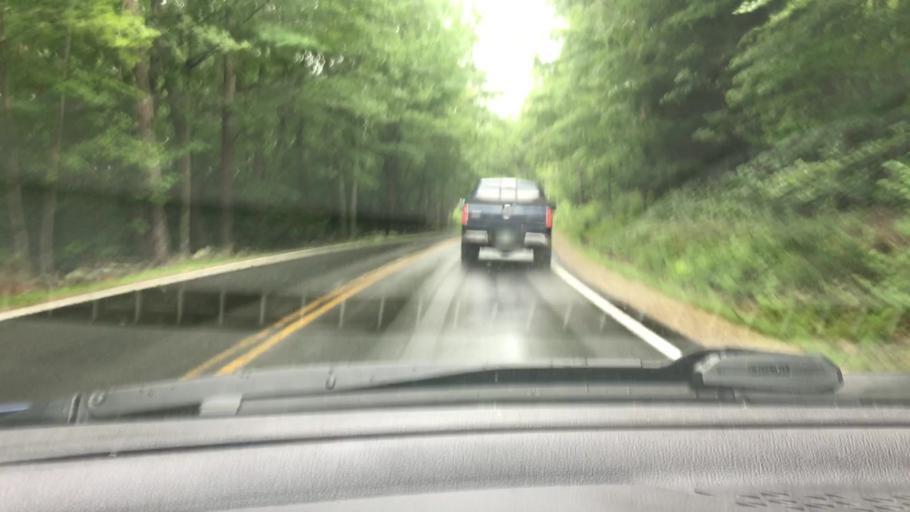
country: US
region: New Hampshire
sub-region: Merrimack County
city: Epsom
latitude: 43.2036
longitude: -71.2747
